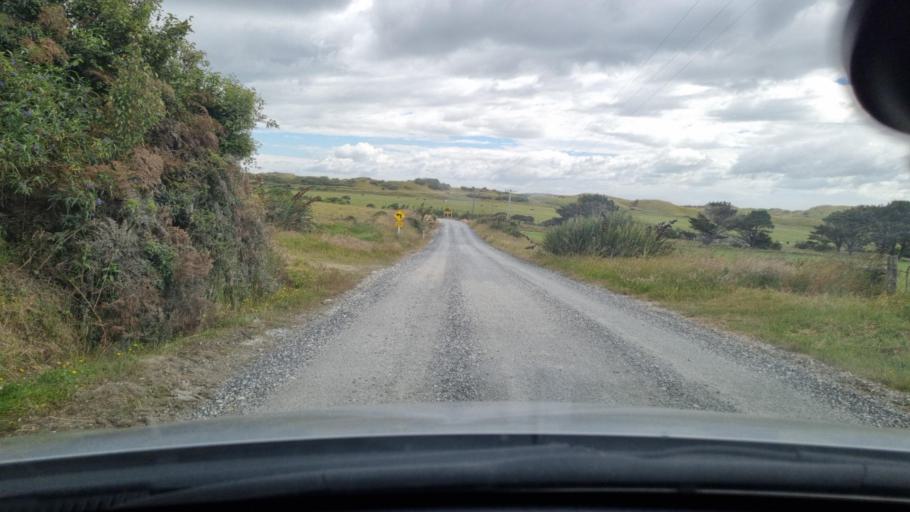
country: NZ
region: Southland
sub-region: Invercargill City
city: Bluff
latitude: -46.5218
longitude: 168.2719
